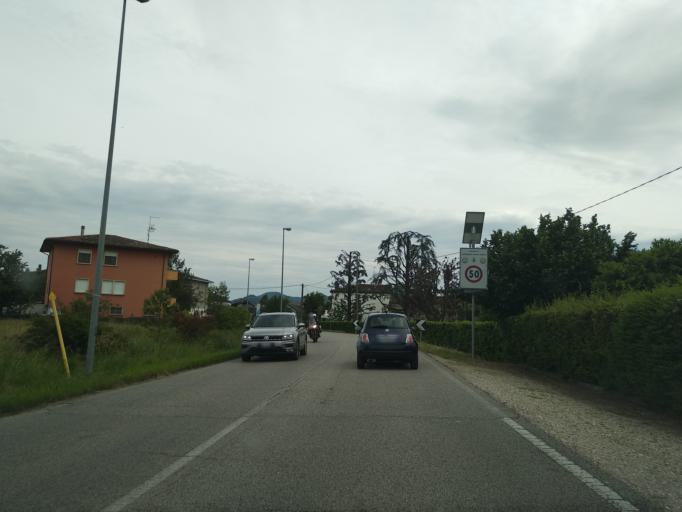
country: IT
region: Veneto
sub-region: Provincia di Padova
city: Montemerlo
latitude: 45.3912
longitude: 11.6974
